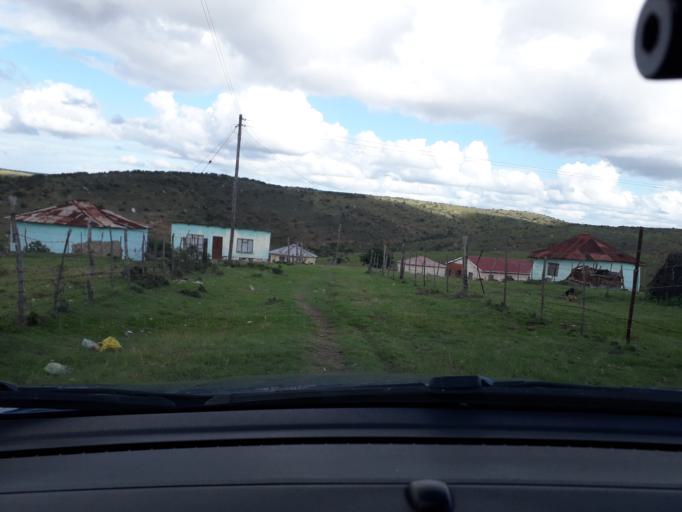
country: ZA
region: Eastern Cape
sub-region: Buffalo City Metropolitan Municipality
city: Bhisho
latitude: -33.1174
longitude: 27.4332
